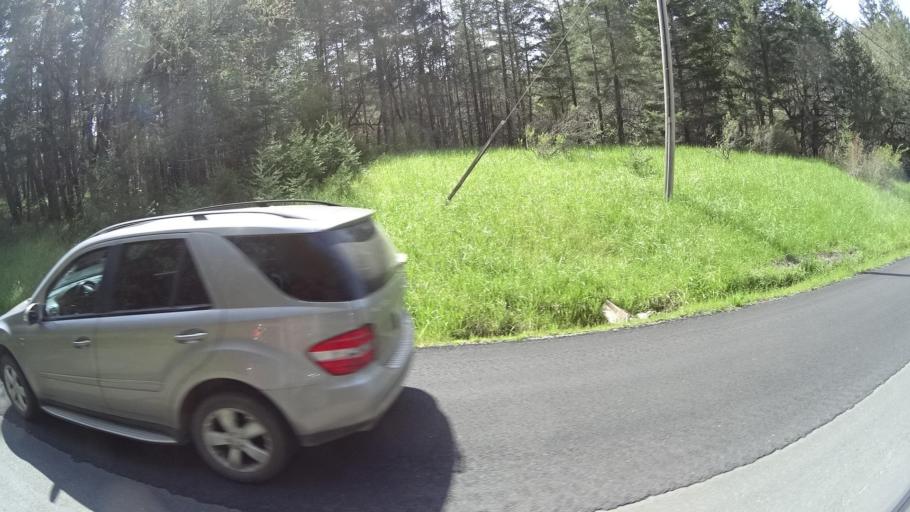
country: US
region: California
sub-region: Humboldt County
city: Redway
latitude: 40.4348
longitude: -123.7688
